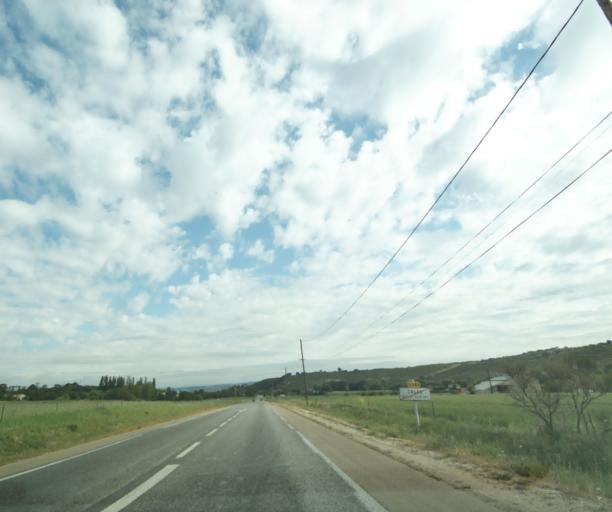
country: FR
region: Provence-Alpes-Cote d'Azur
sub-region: Departement des Bouches-du-Rhone
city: Cabries
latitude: 43.4703
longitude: 5.3546
